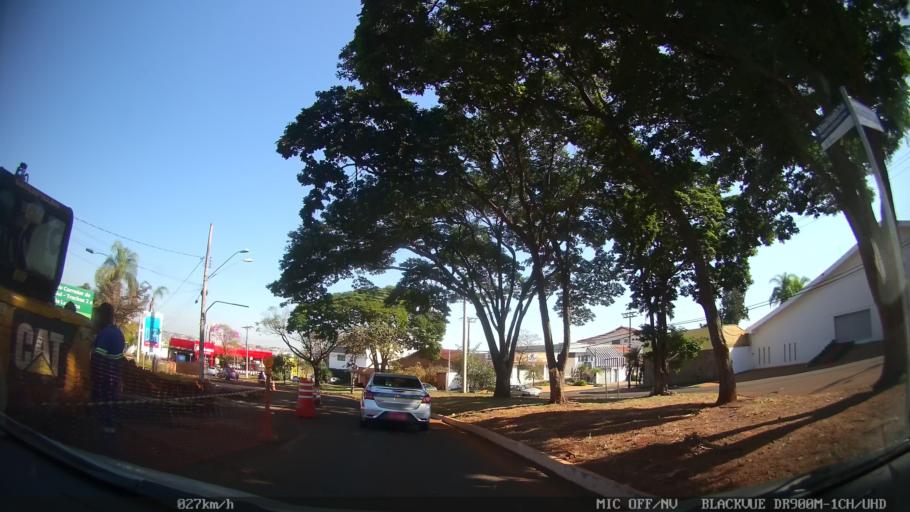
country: BR
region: Sao Paulo
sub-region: Ribeirao Preto
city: Ribeirao Preto
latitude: -21.1988
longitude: -47.8161
